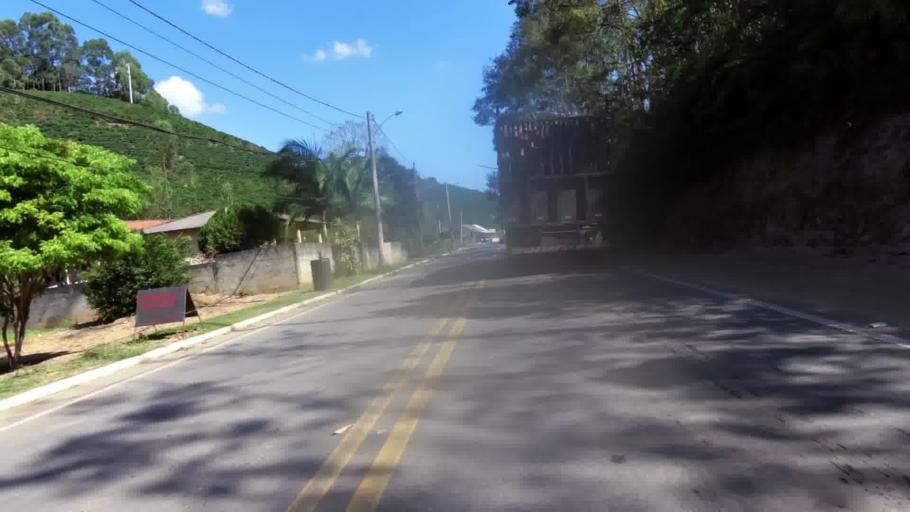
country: BR
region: Espirito Santo
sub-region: Marechal Floriano
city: Marechal Floriano
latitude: -20.4404
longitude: -40.7785
